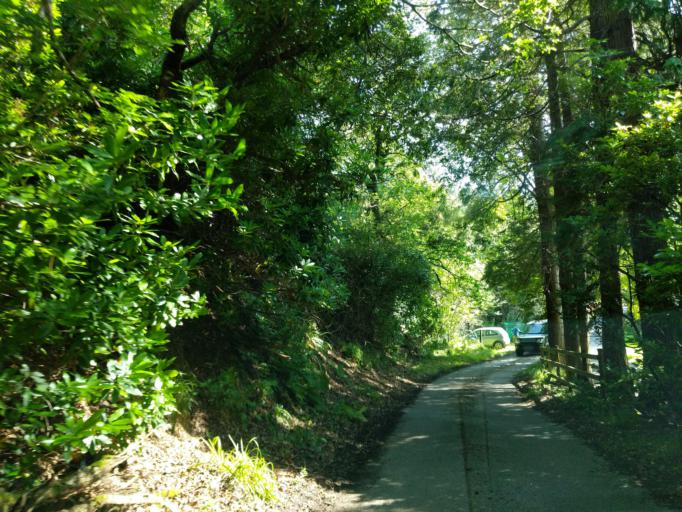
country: GB
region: Scotland
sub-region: Moray
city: Fochabers
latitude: 57.5523
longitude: -3.1375
